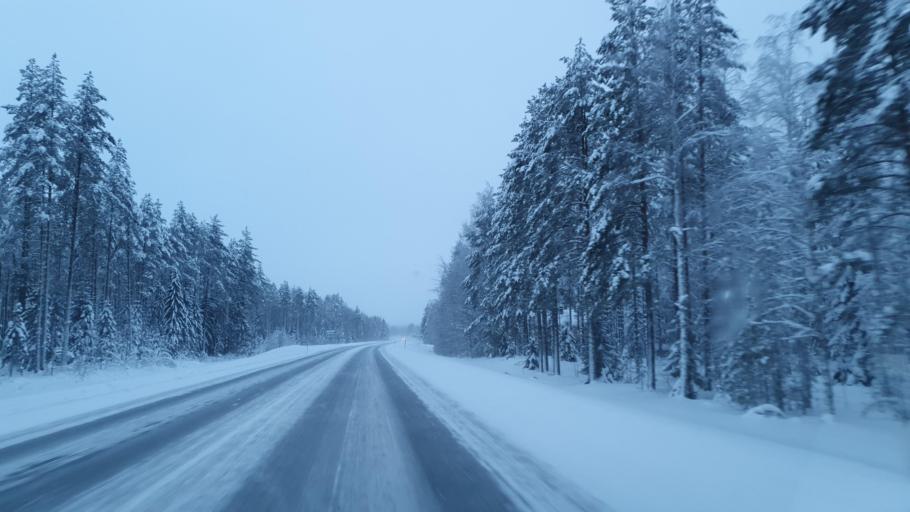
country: FI
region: Kainuu
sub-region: Kajaani
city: Vaala
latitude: 64.5547
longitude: 27.0414
